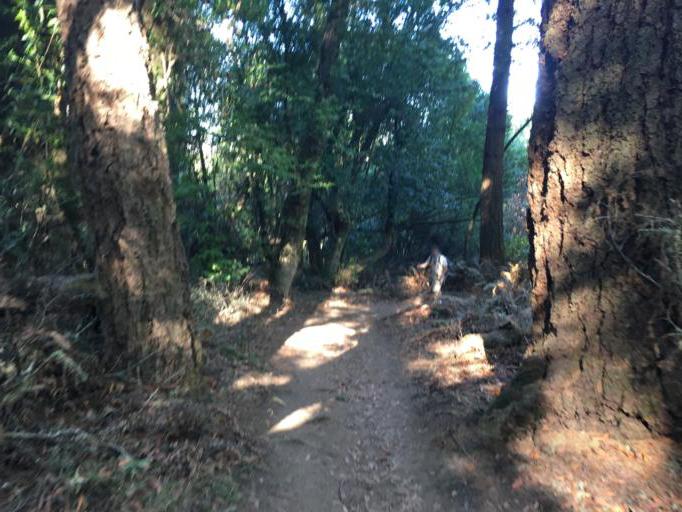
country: US
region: California
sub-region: Marin County
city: Inverness
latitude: 38.0368
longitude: -122.8073
